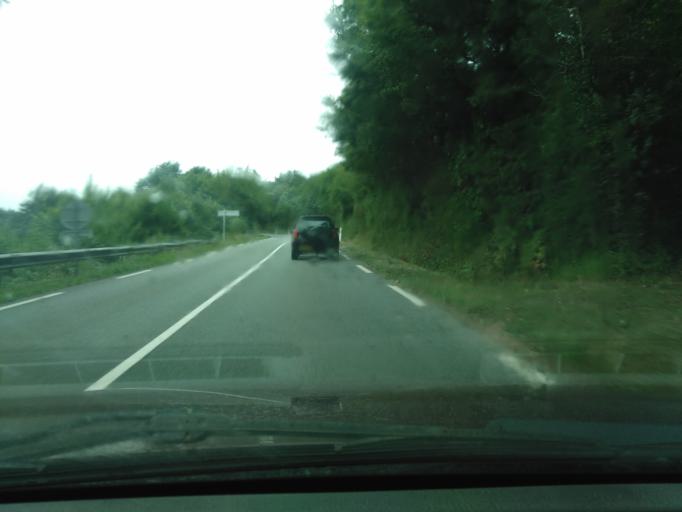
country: FR
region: Pays de la Loire
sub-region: Departement de la Vendee
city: Bournezeau
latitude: 46.5909
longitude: -1.1180
